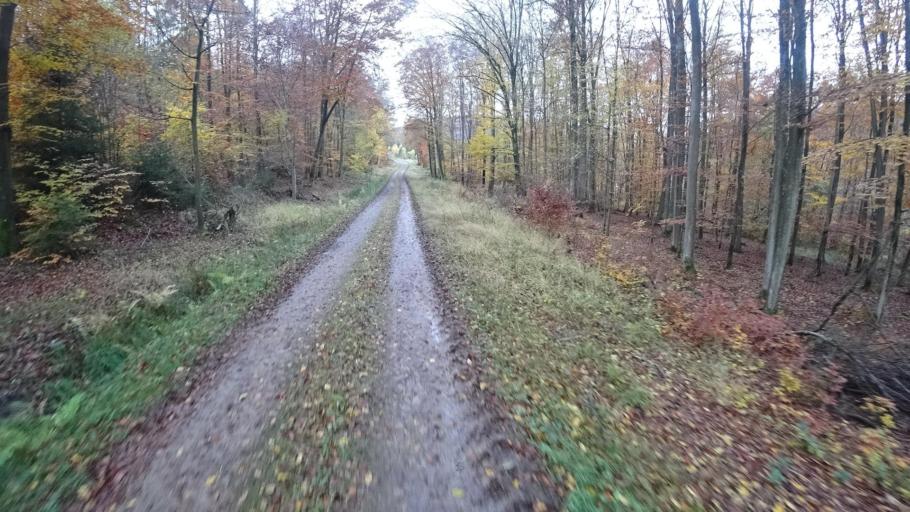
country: DE
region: Rheinland-Pfalz
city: Damscheid
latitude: 50.1192
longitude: 7.6643
